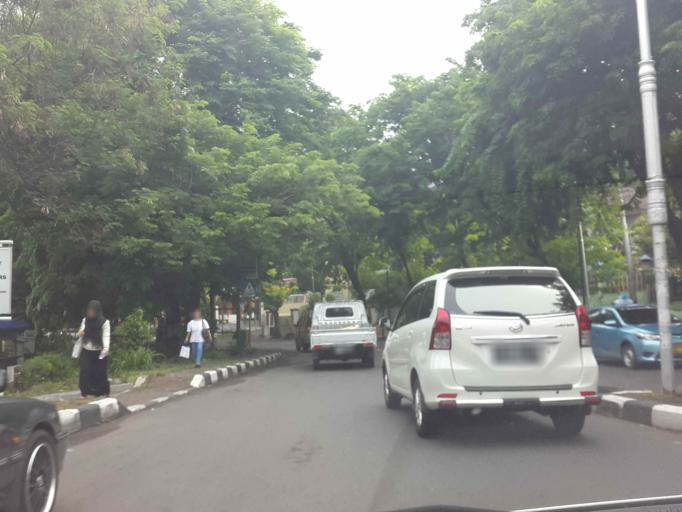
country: ID
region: Central Java
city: Semarang
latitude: -6.9958
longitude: 110.4102
